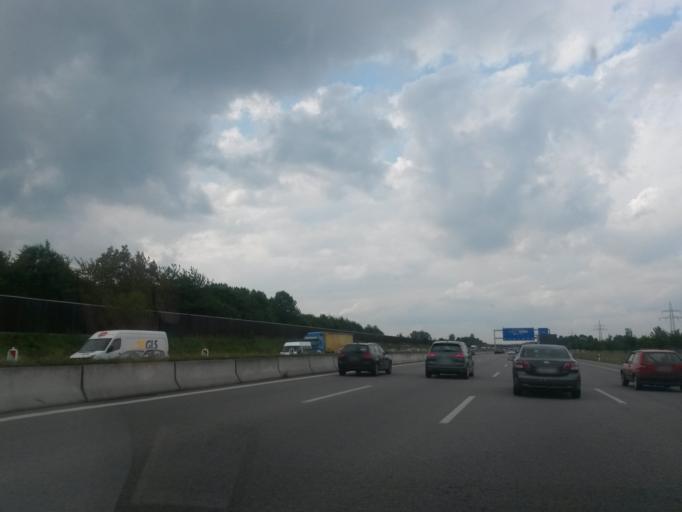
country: DE
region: Bavaria
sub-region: Upper Bavaria
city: Eching
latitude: 48.2895
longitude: 11.6368
